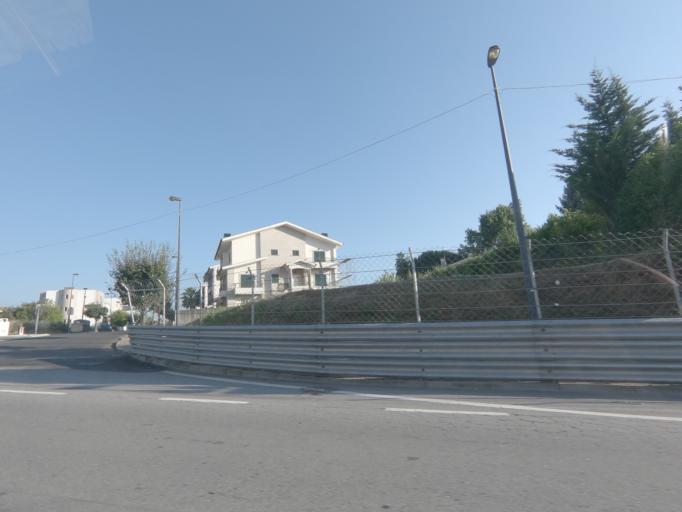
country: PT
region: Vila Real
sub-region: Vila Real
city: Vila Real
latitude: 41.3054
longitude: -7.7230
